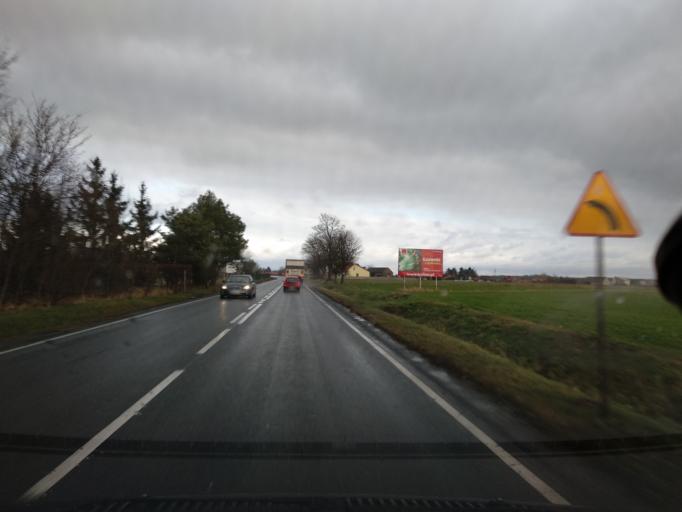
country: PL
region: Greater Poland Voivodeship
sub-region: Powiat koninski
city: Stare Miasto
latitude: 52.1505
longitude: 18.2025
